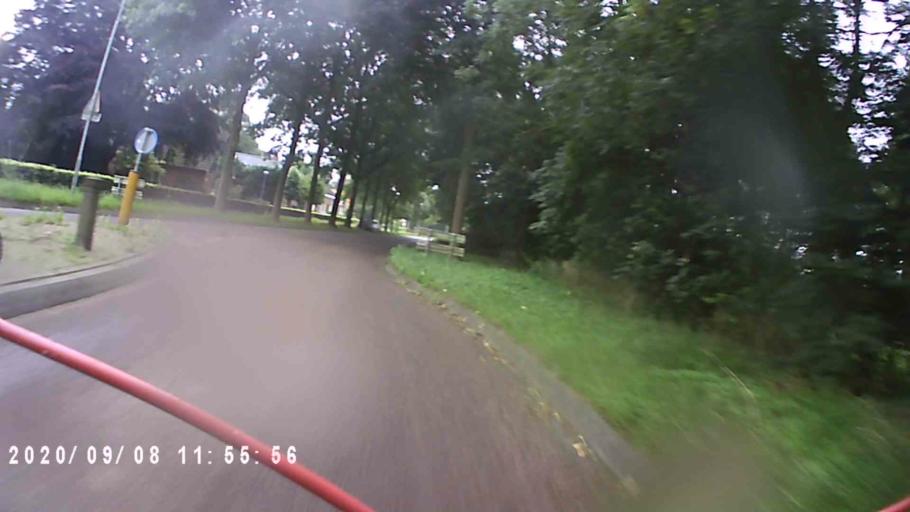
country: NL
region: Groningen
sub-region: Gemeente Veendam
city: Veendam
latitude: 53.1126
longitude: 6.8223
